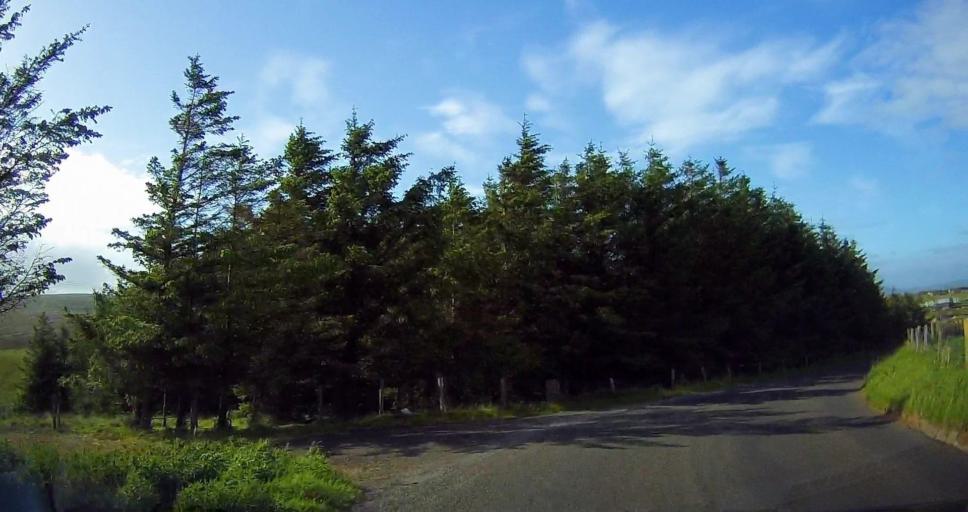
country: GB
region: Scotland
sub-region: Orkney Islands
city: Stromness
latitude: 58.8241
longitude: -3.2105
